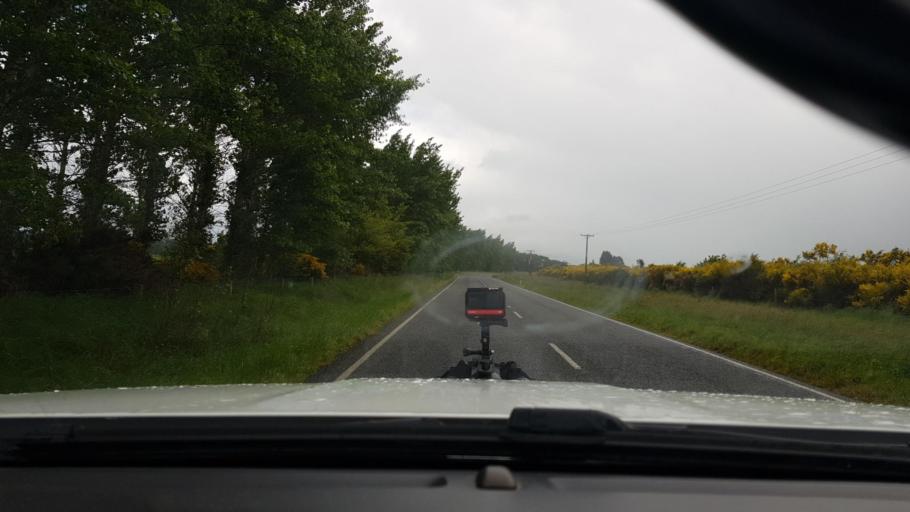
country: NZ
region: Southland
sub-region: Southland District
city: Winton
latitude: -45.7287
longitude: 168.3935
